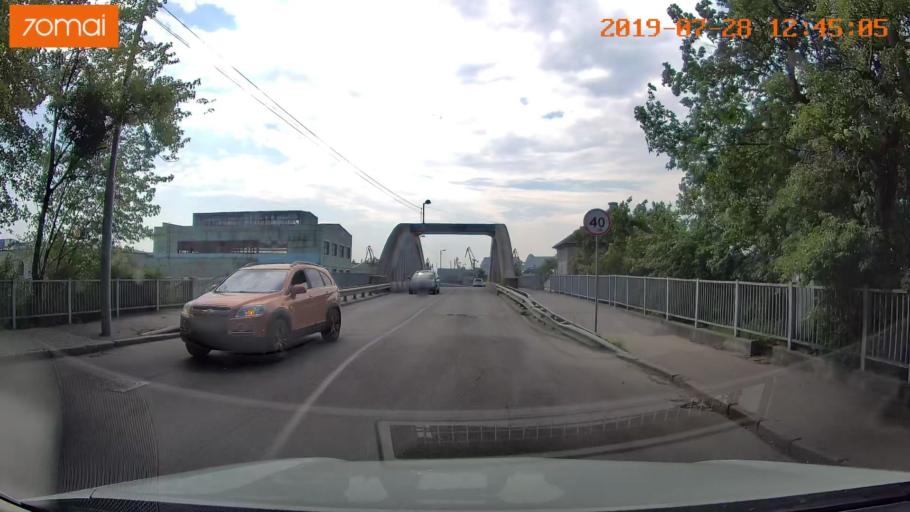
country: RU
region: Kaliningrad
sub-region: Gorod Kaliningrad
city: Kaliningrad
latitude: 54.7111
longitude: 20.4584
